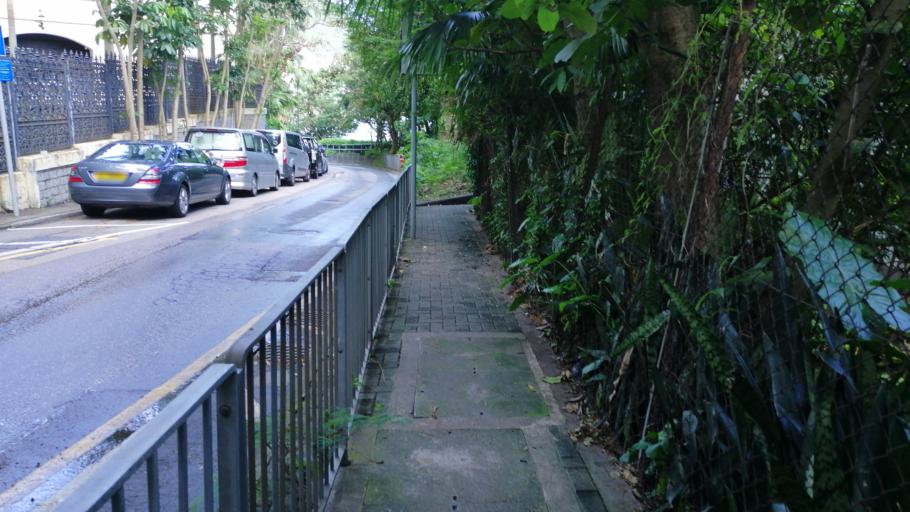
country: HK
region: Wanchai
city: Wan Chai
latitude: 22.2391
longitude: 114.1935
